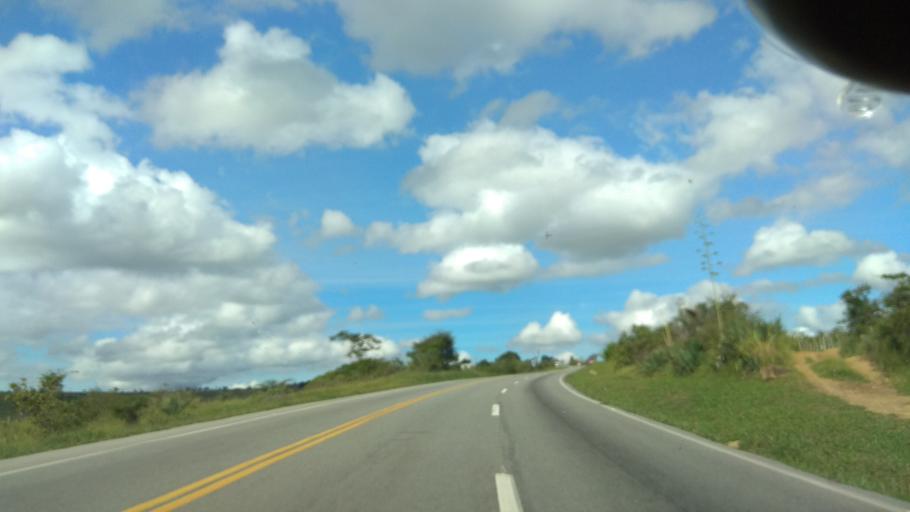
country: BR
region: Bahia
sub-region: Santa Ines
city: Santa Ines
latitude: -13.1056
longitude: -39.9807
